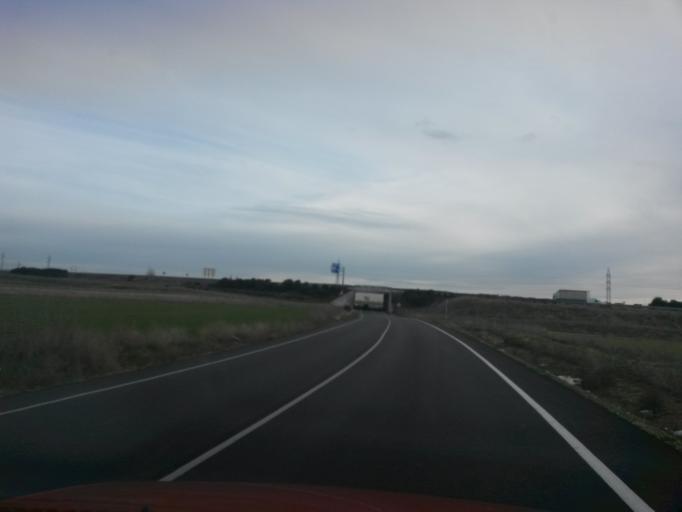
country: ES
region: Castille and Leon
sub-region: Provincia de Salamanca
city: Villares de la Reina
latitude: 41.0012
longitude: -5.6415
